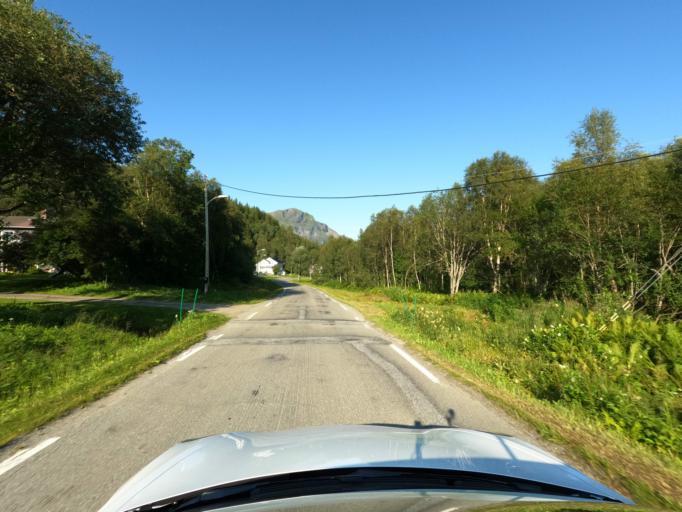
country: NO
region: Nordland
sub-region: Narvik
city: Bjerkvik
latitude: 68.5571
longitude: 17.6196
